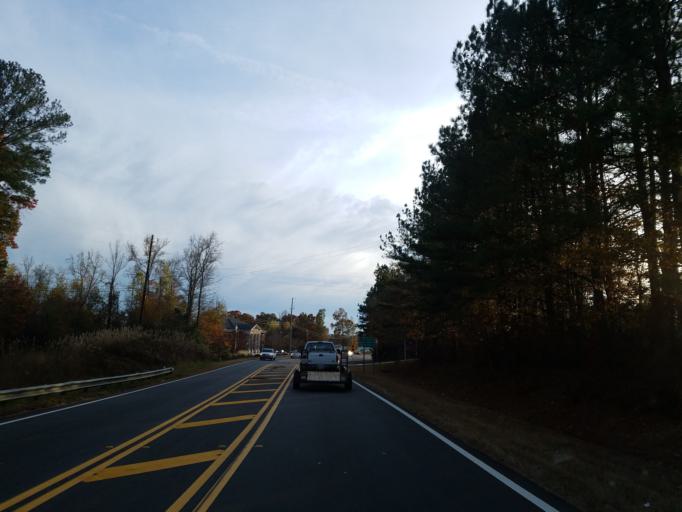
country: US
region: Georgia
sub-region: Haralson County
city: Bremen
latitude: 33.7127
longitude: -85.1599
